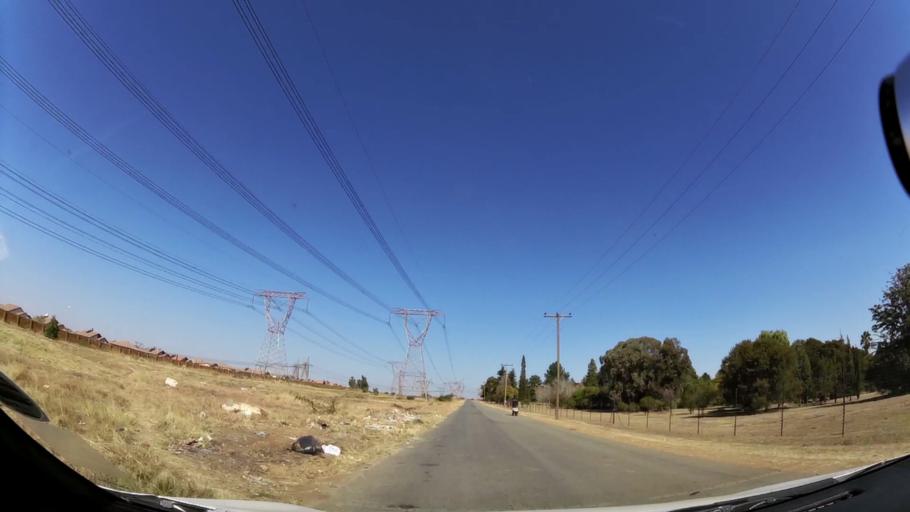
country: ZA
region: Gauteng
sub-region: City of Johannesburg Metropolitan Municipality
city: Diepsloot
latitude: -25.9003
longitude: 28.0855
